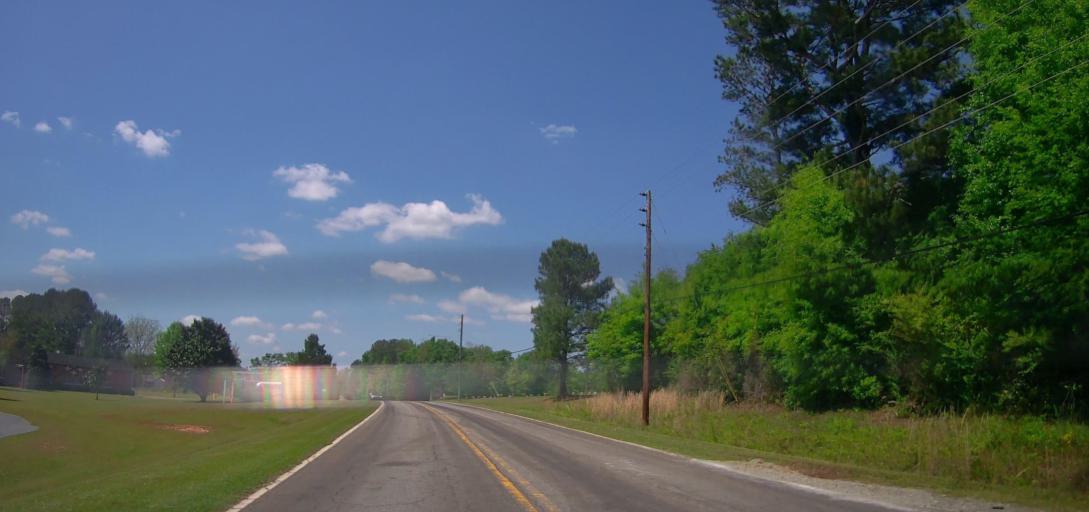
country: US
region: Georgia
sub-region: Putnam County
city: Eatonton
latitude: 33.3279
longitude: -83.4017
